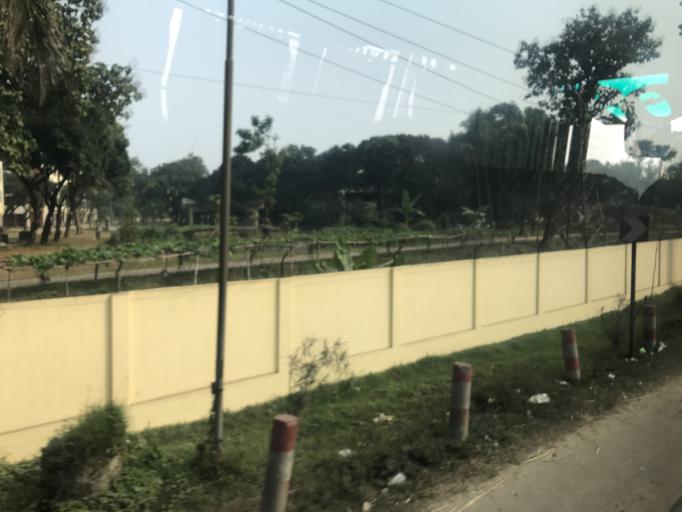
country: BD
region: Dhaka
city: Tungi
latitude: 23.9041
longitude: 90.2681
